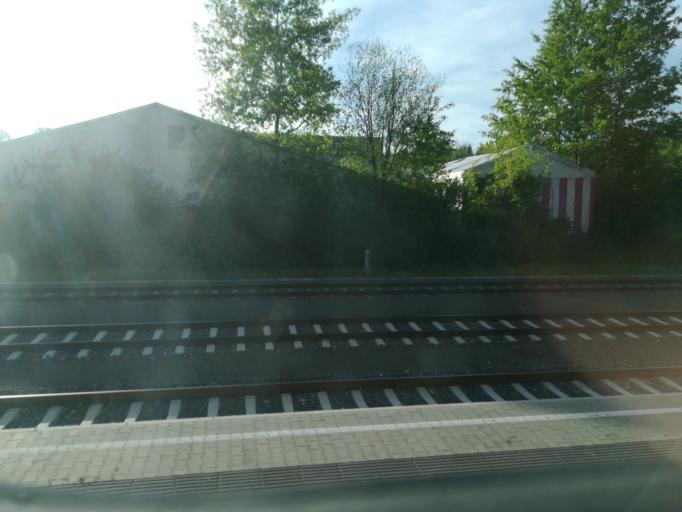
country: AT
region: Styria
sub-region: Politischer Bezirk Graz-Umgebung
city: Unterpremstatten
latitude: 46.9780
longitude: 15.3906
